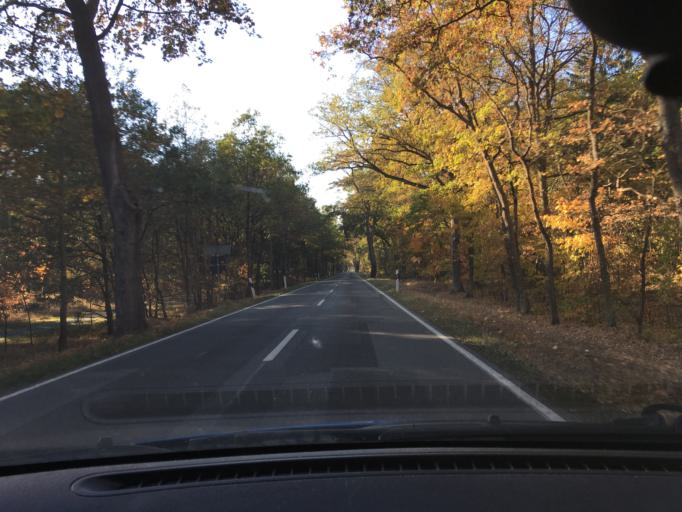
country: DE
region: Mecklenburg-Vorpommern
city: Domitz
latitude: 53.1530
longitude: 11.2299
